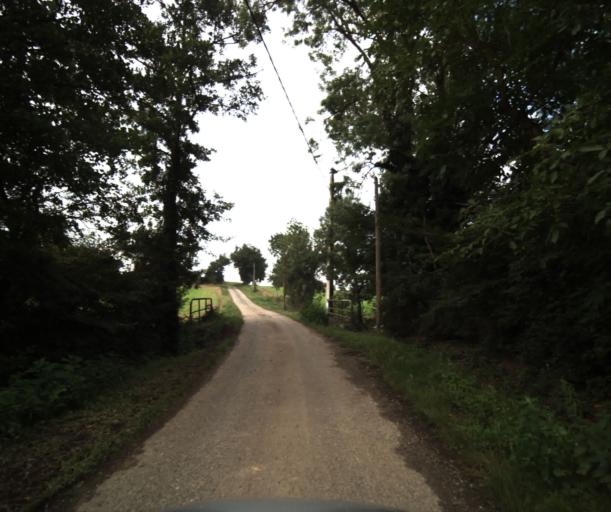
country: FR
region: Midi-Pyrenees
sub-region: Departement de la Haute-Garonne
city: Lacasse
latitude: 43.3899
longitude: 1.2384
